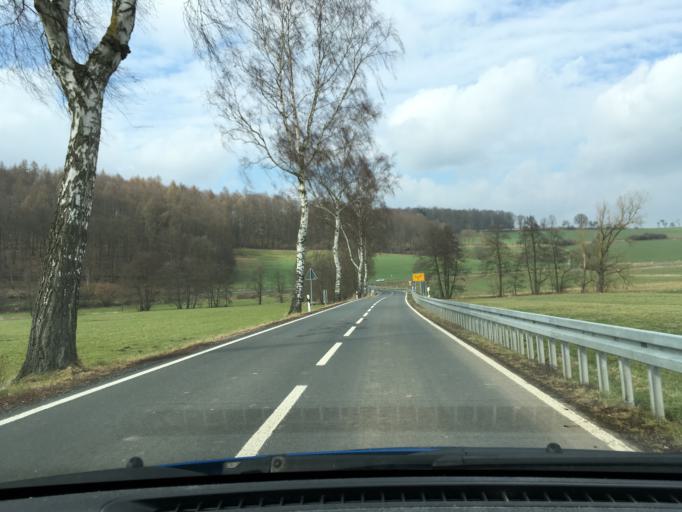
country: DE
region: Lower Saxony
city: Adelebsen
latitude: 51.5717
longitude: 9.7193
